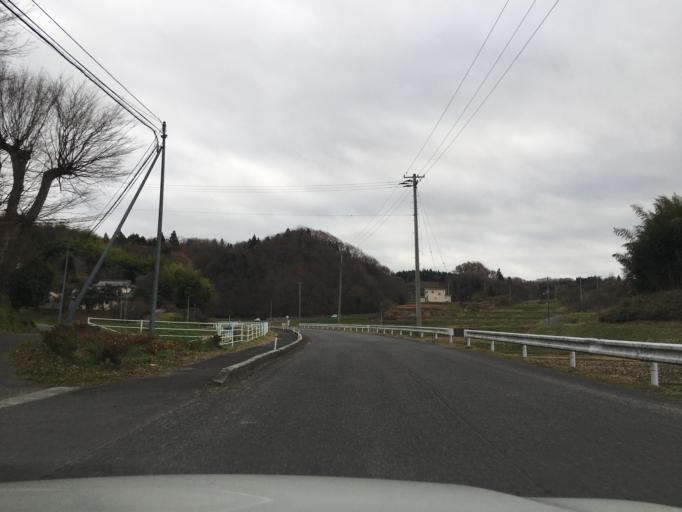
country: JP
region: Fukushima
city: Funehikimachi-funehiki
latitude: 37.4762
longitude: 140.5469
